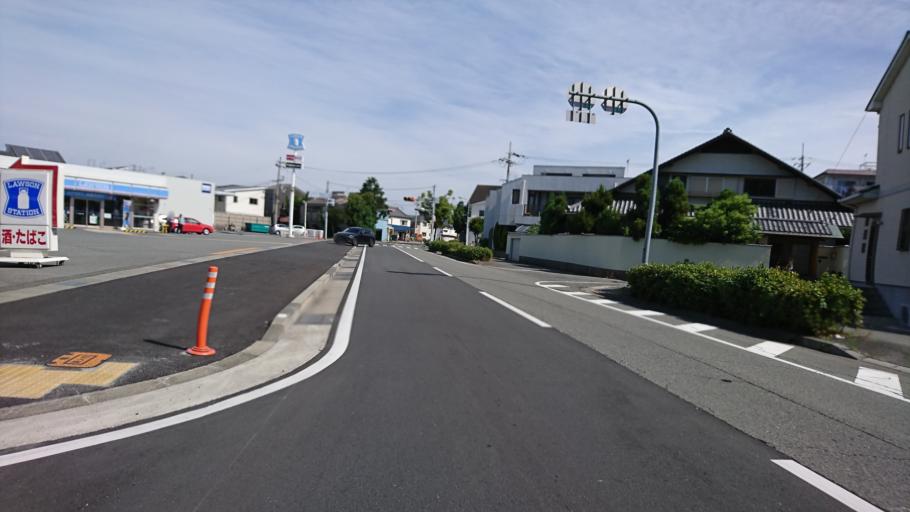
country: JP
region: Hyogo
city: Himeji
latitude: 34.8304
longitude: 134.7149
